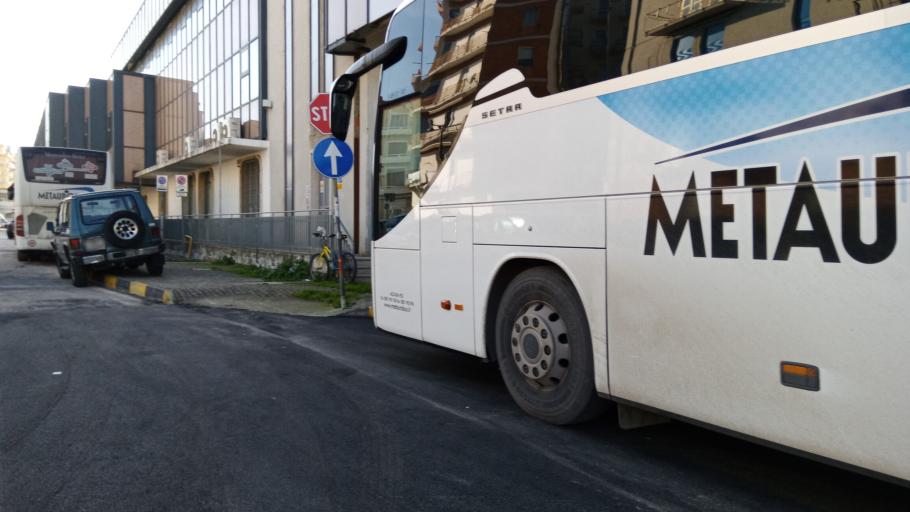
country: IT
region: Molise
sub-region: Provincia di Campobasso
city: Termoli
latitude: 42.0021
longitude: 14.9919
